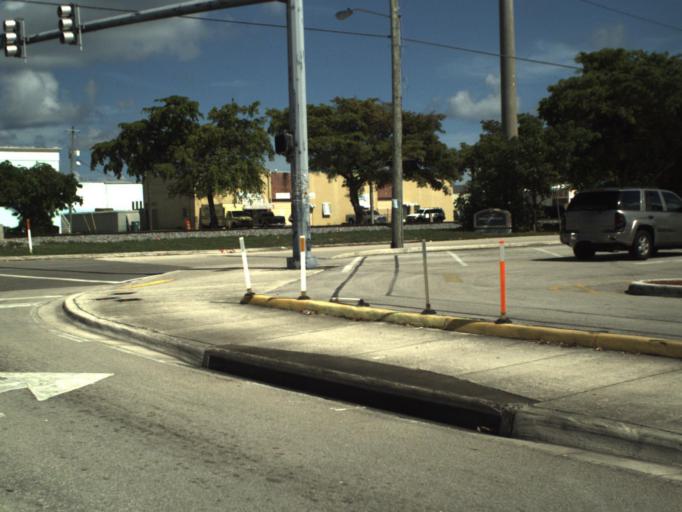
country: US
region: Florida
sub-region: Broward County
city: Dania Beach
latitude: 26.0334
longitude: -80.1503
